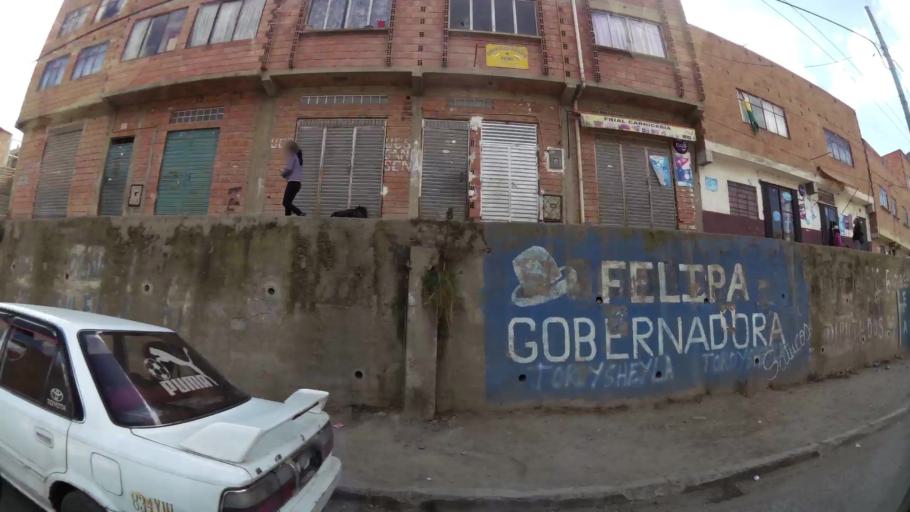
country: BO
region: La Paz
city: La Paz
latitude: -16.4606
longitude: -68.1062
